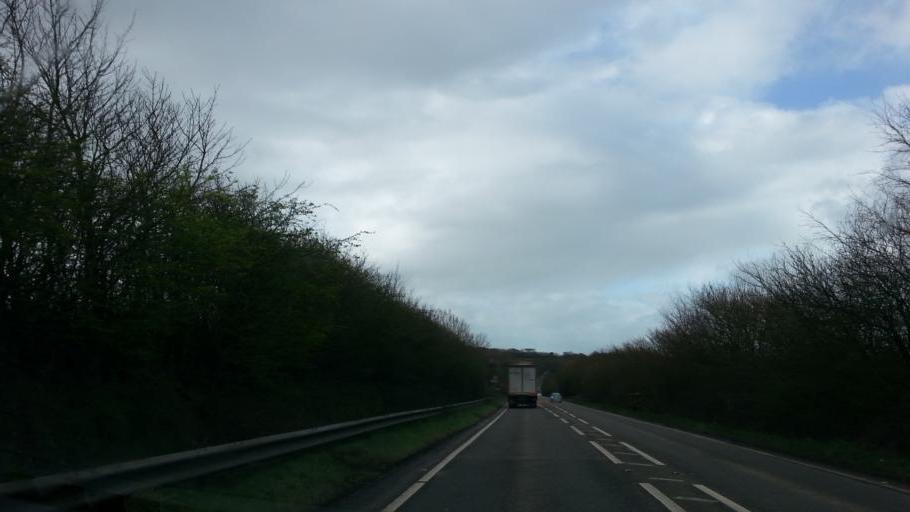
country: GB
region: England
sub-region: Devon
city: Northam
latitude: 51.0185
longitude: -4.2385
